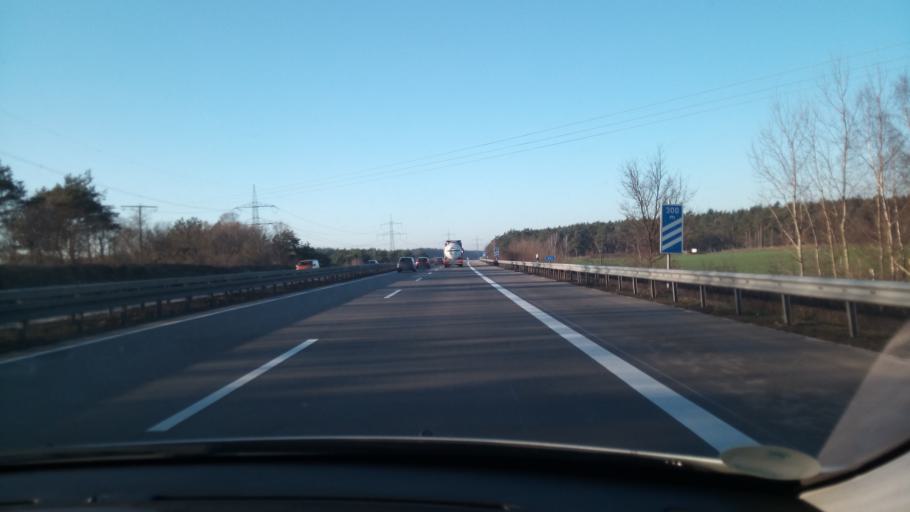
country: DE
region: Schleswig-Holstein
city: Besenthal
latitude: 53.5362
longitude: 10.7367
